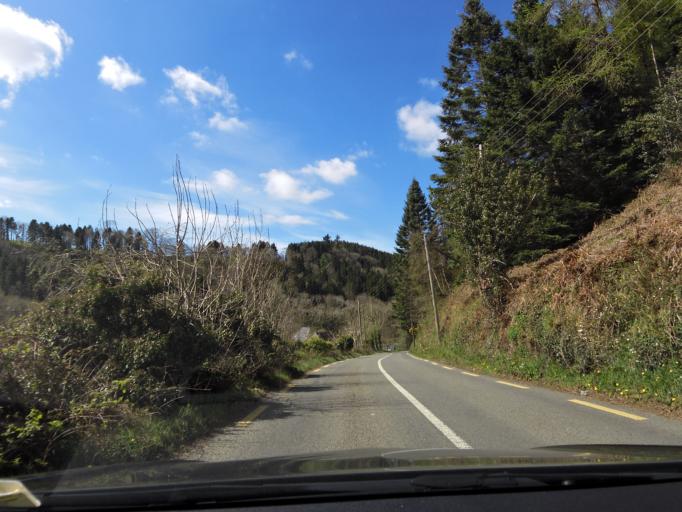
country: IE
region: Leinster
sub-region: Wicklow
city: Aughrim
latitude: 52.8350
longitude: -6.2485
